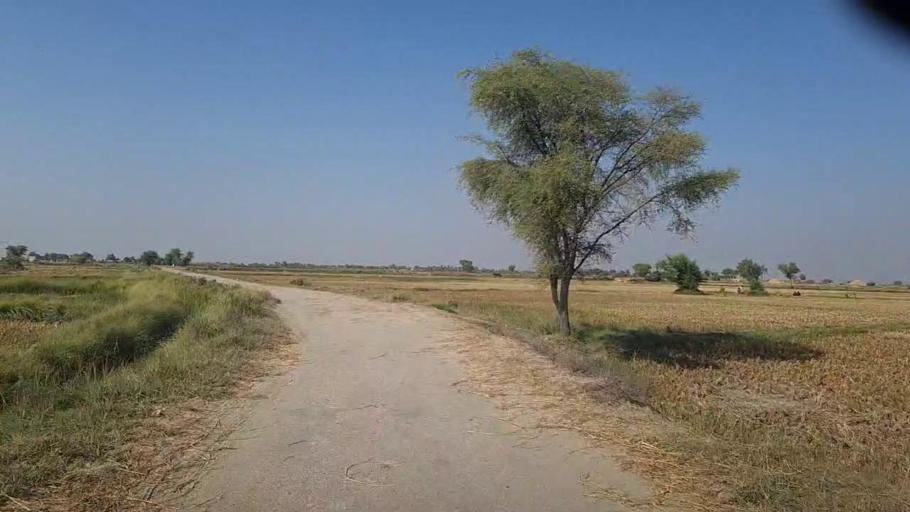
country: PK
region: Sindh
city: Tangwani
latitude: 28.2617
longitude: 68.9342
